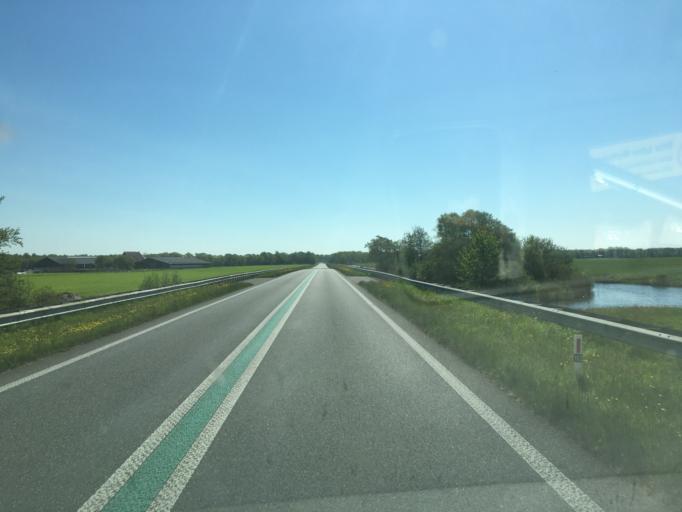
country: NL
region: Friesland
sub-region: Gemeente Gaasterlan-Sleat
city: Oudemirdum
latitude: 52.8802
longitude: 5.5007
